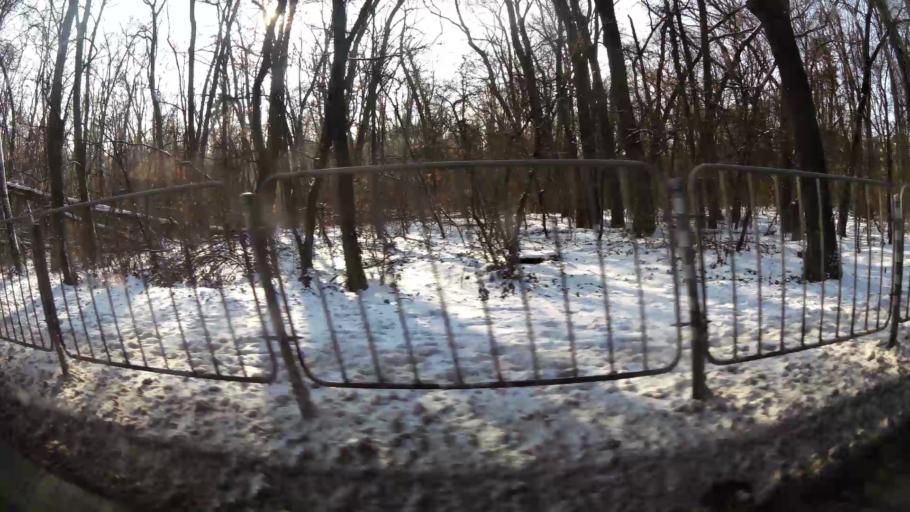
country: BG
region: Sofia-Capital
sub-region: Stolichna Obshtina
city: Sofia
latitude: 42.6717
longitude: 23.3368
